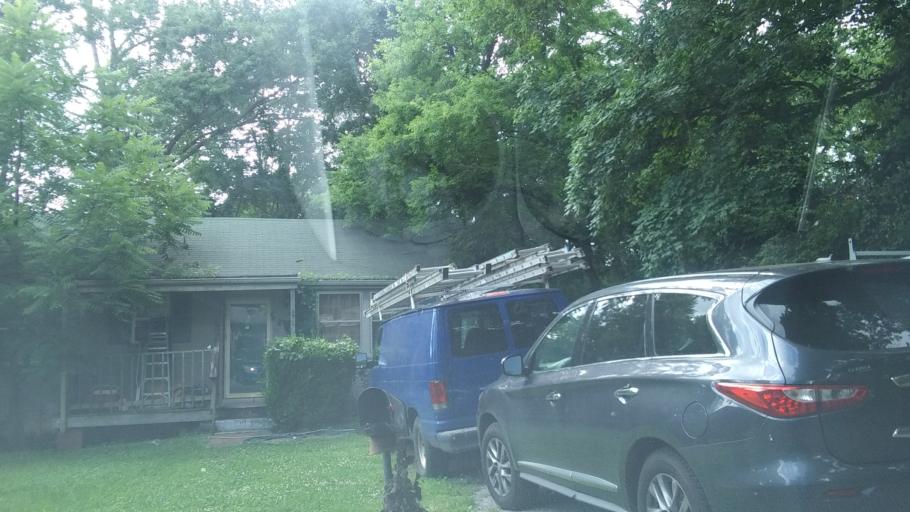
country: US
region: Tennessee
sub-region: Davidson County
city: Oak Hill
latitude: 36.0657
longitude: -86.7149
